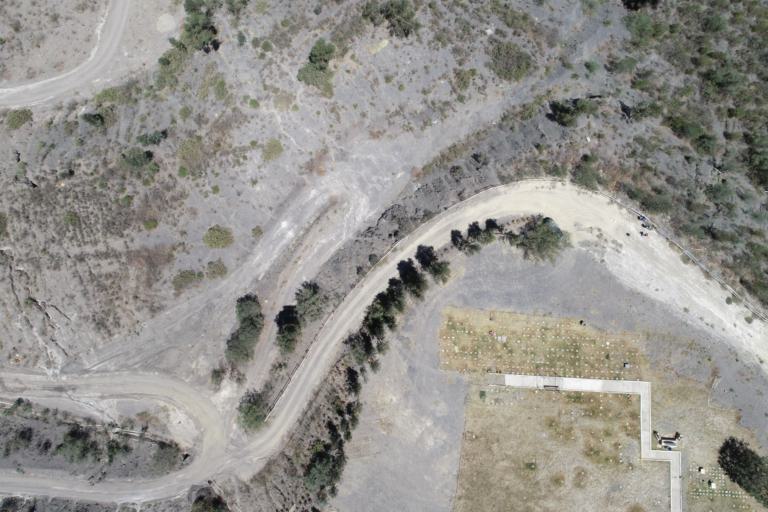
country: BO
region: La Paz
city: La Paz
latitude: -16.6138
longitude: -68.0616
